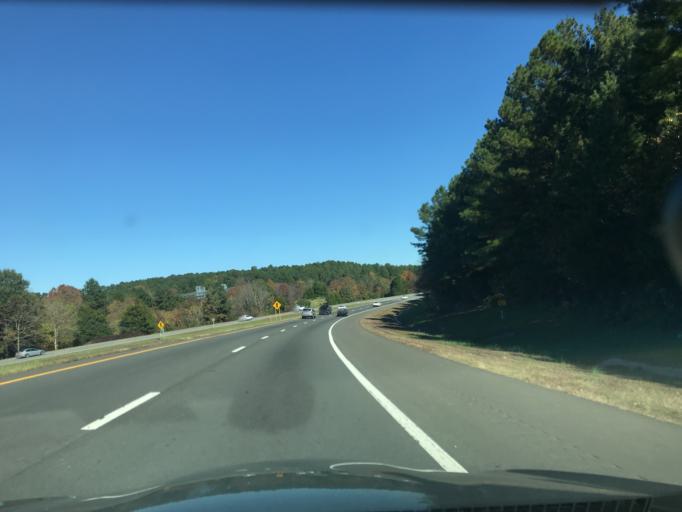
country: US
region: North Carolina
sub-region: Wake County
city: Morrisville
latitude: 35.9034
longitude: -78.8709
